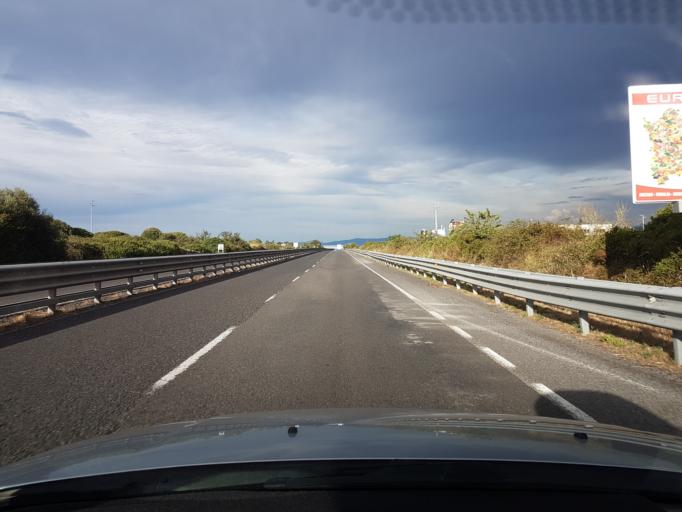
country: IT
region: Sardinia
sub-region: Provincia di Oristano
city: Paulilatino
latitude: 40.0924
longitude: 8.7628
